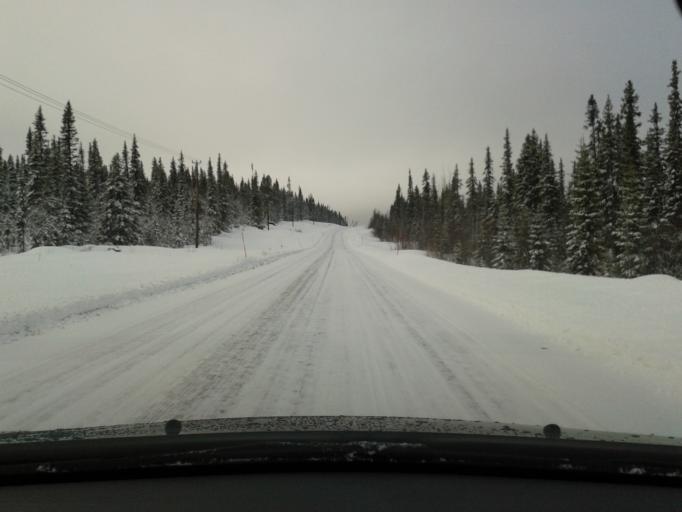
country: SE
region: Vaesterbotten
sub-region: Vilhelmina Kommun
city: Sjoberg
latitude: 65.2088
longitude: 16.0084
